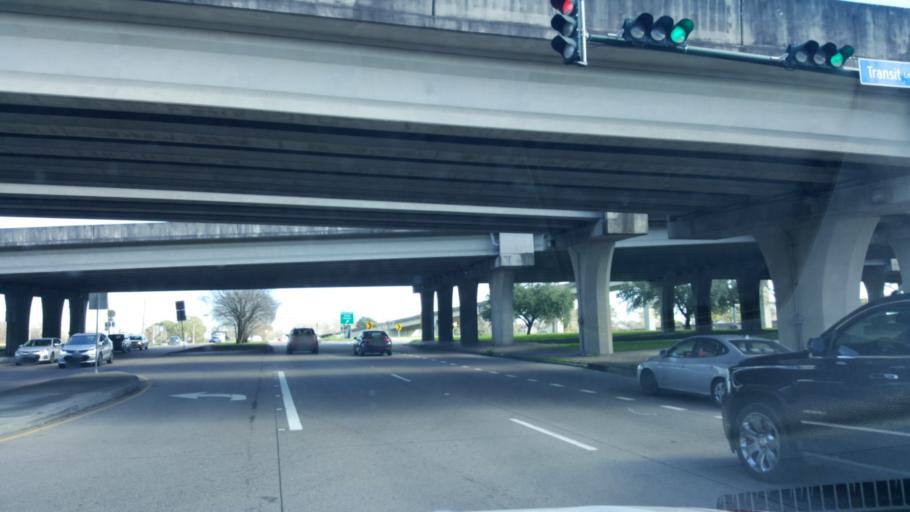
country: US
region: Louisiana
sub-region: Jefferson Parish
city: Terrytown
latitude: 29.9305
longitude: -90.0382
